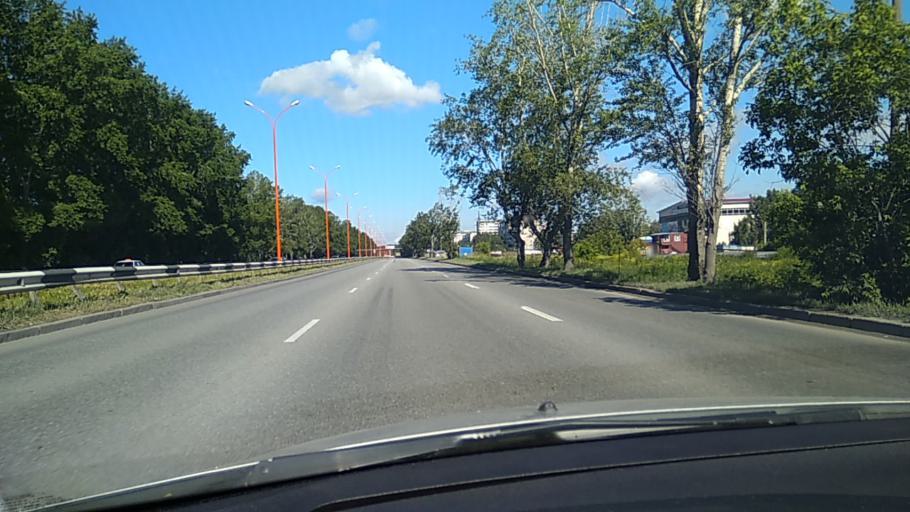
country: RU
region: Sverdlovsk
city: Sovkhoznyy
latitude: 56.7958
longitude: 60.5624
